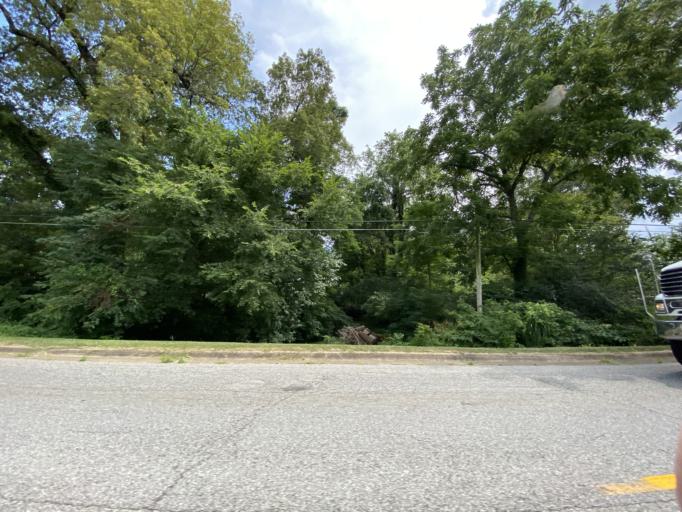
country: US
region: Missouri
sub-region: Oregon County
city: Thayer
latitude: 36.4957
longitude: -91.5454
